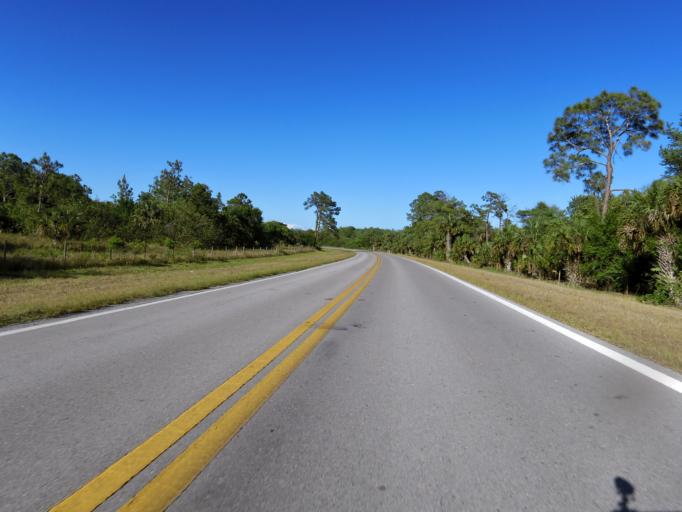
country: US
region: Florida
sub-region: Collier County
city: Immokalee
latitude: 26.2962
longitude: -81.3635
